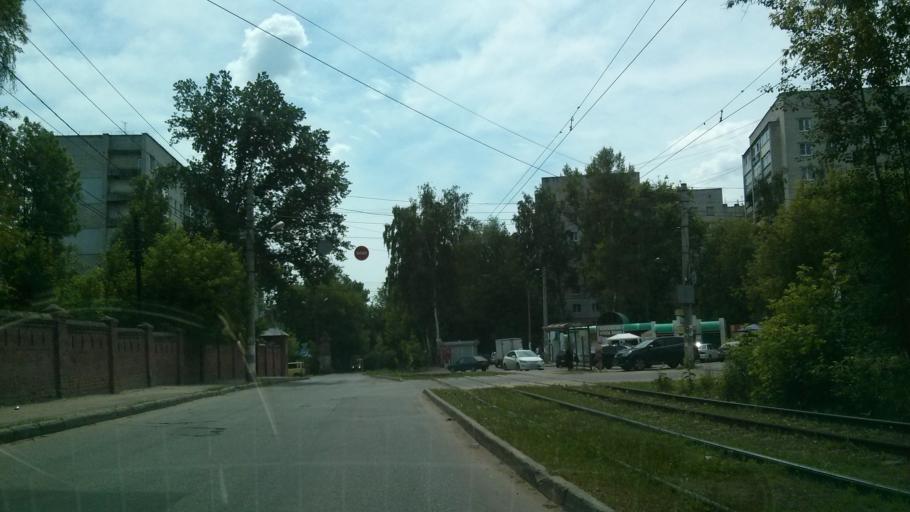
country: RU
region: Nizjnij Novgorod
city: Nizhniy Novgorod
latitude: 56.2990
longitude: 43.9917
